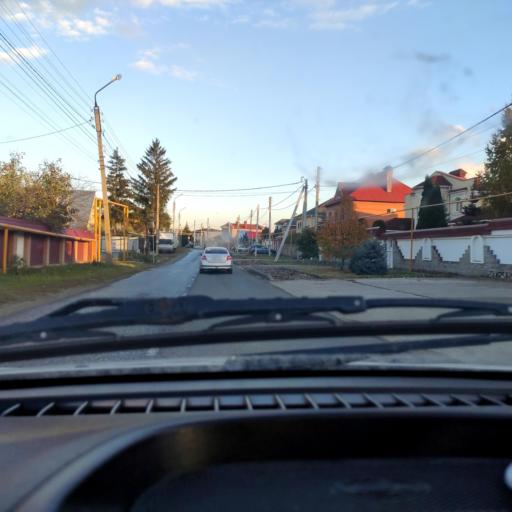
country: RU
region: Samara
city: Zhigulevsk
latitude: 53.4643
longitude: 49.6256
